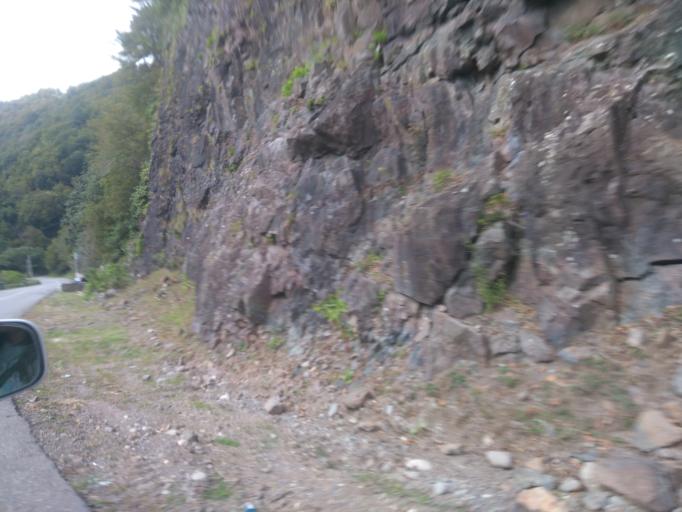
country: GE
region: Ajaria
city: Khelvachauri
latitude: 41.5434
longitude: 41.7160
